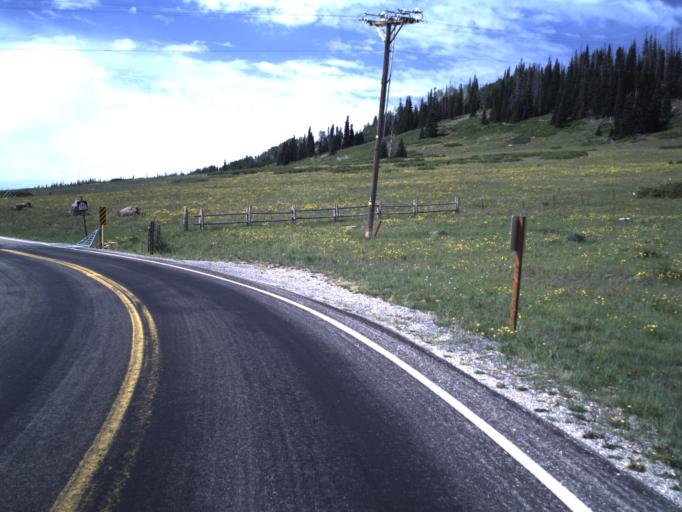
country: US
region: Utah
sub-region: Iron County
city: Cedar City
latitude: 37.6055
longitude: -112.8508
